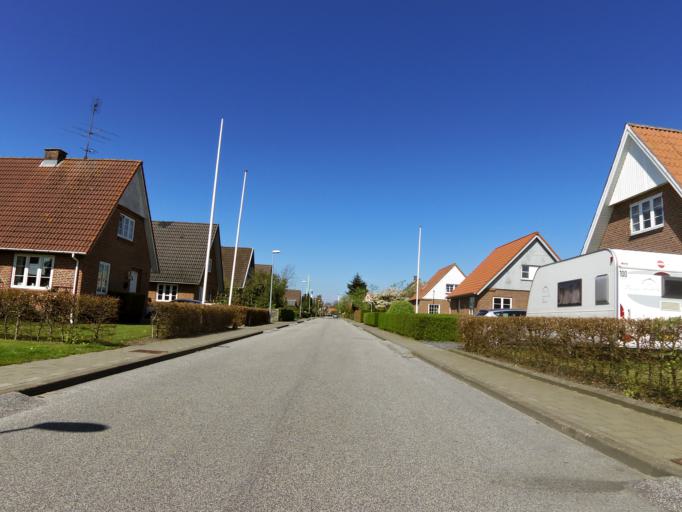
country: DK
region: South Denmark
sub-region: Tonder Kommune
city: Sherrebek
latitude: 55.1529
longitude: 8.7708
